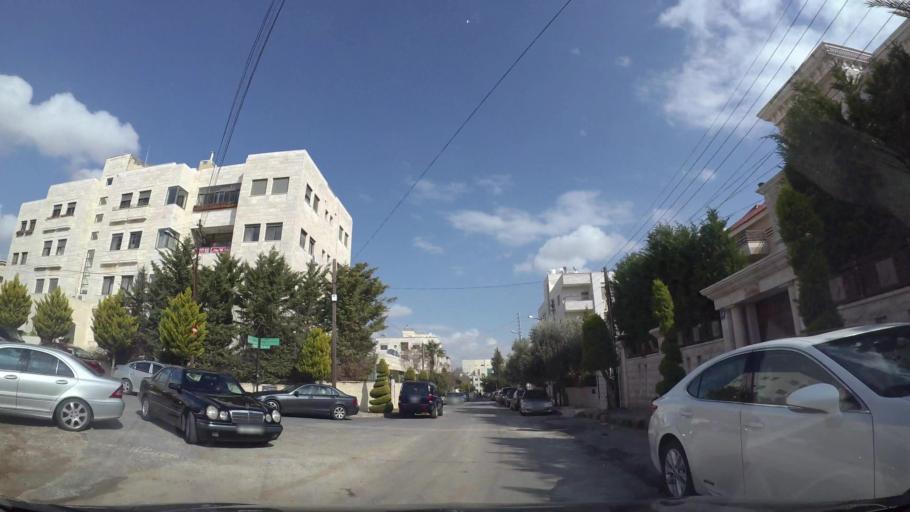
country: JO
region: Amman
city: Amman
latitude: 31.9691
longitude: 35.8908
